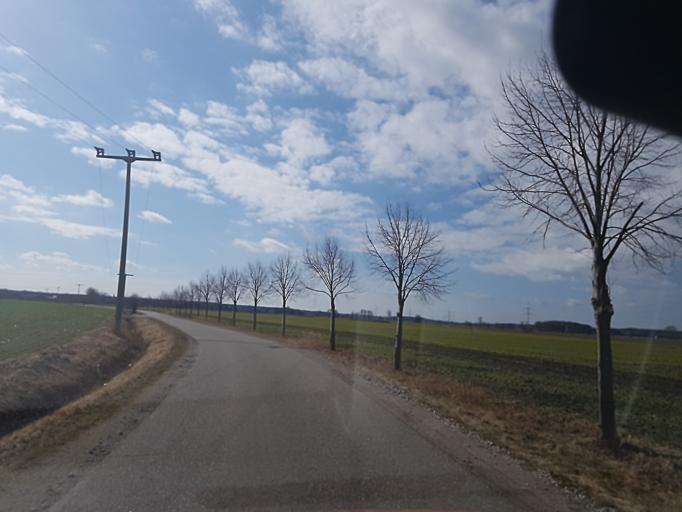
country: DE
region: Brandenburg
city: Ruckersdorf
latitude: 51.5774
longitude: 13.5259
